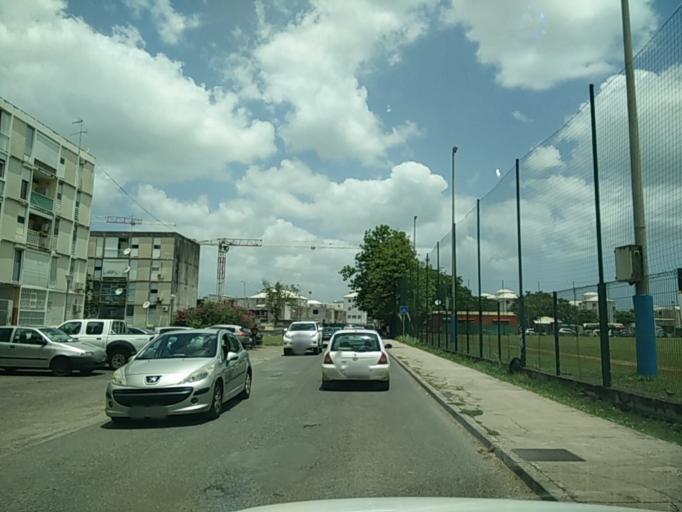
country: GP
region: Guadeloupe
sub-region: Guadeloupe
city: Pointe-a-Pitre
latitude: 16.2563
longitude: -61.5318
